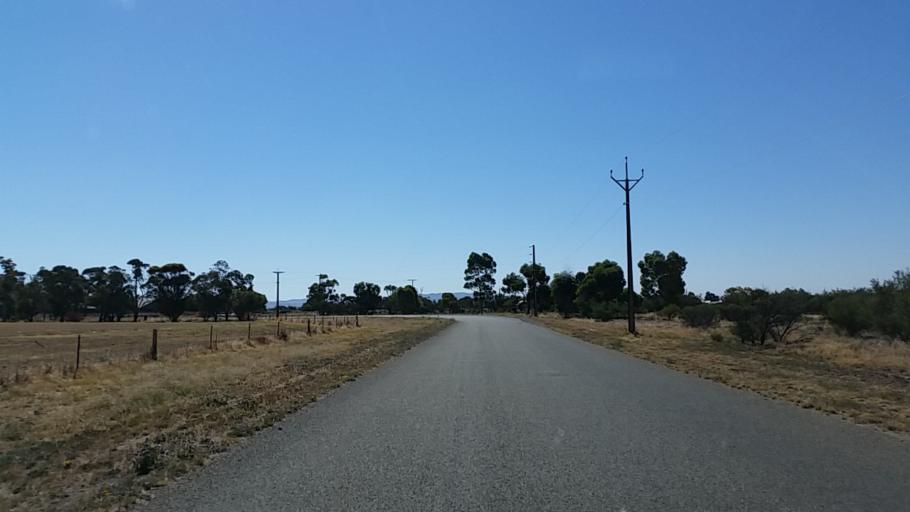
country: AU
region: South Australia
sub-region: Peterborough
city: Peterborough
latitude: -32.7346
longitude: 138.6217
